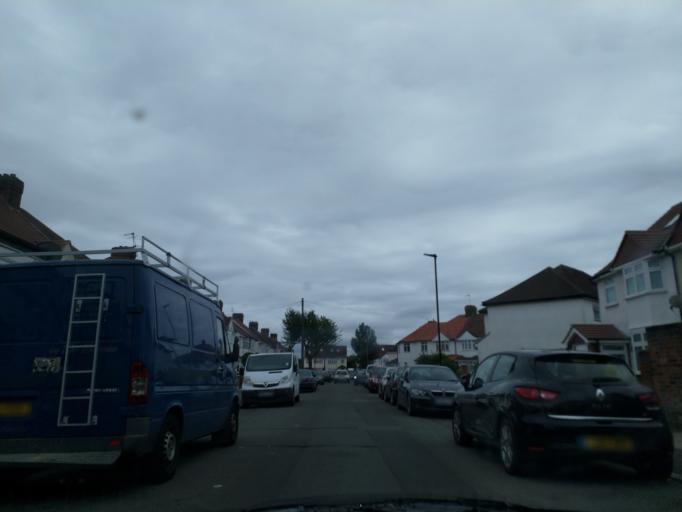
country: GB
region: England
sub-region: Greater London
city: Hounslow
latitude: 51.4641
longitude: -0.3821
